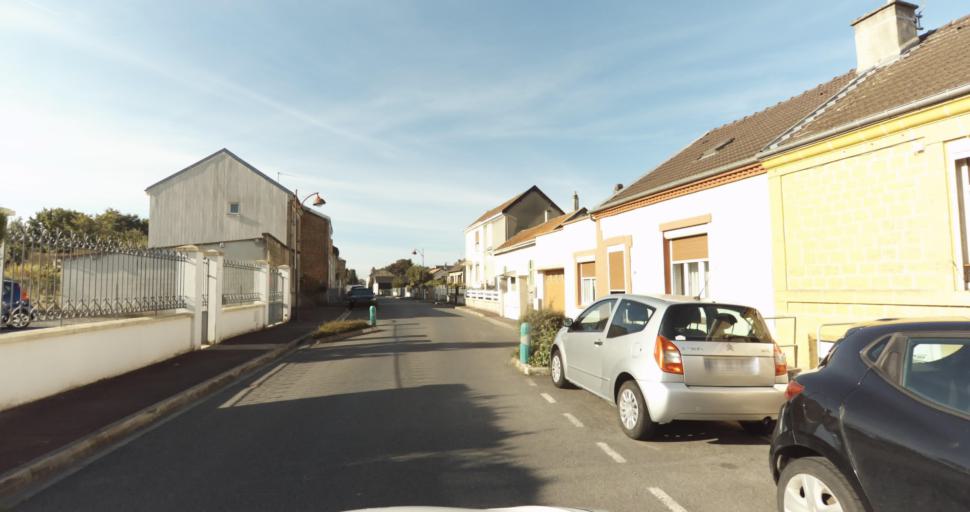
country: FR
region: Champagne-Ardenne
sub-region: Departement des Ardennes
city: Villers-Semeuse
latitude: 49.7461
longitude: 4.7383
